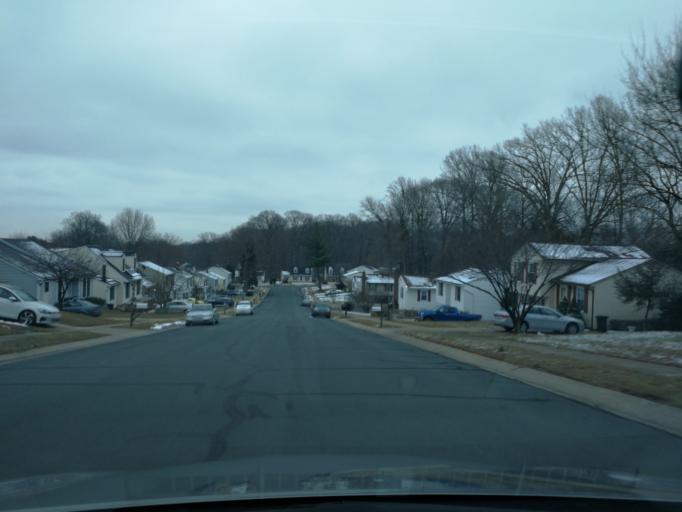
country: US
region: Maryland
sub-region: Harford County
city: Bel Air South
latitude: 39.4875
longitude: -76.3064
